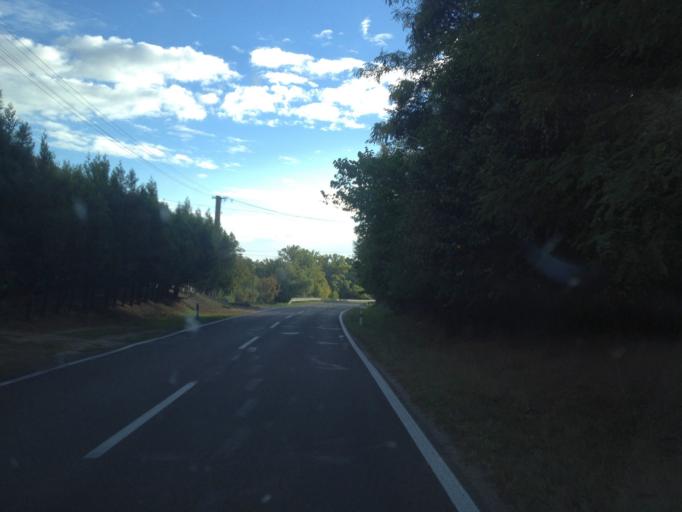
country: HU
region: Komarom-Esztergom
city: Dunaalmas
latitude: 47.7462
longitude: 18.3299
